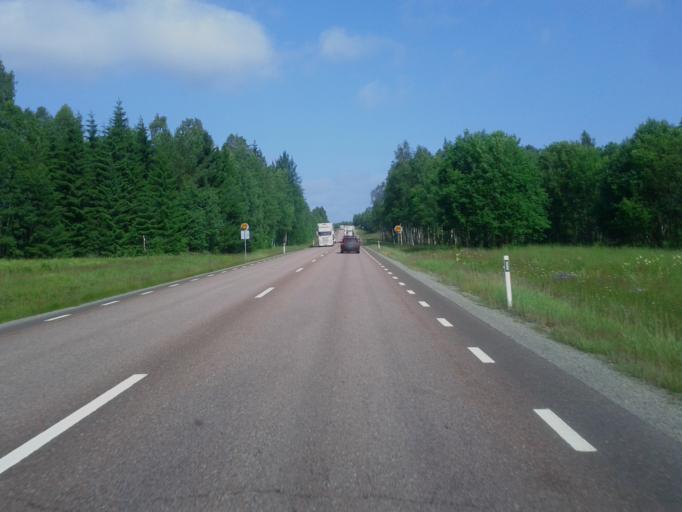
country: SE
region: Vaesterbotten
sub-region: Skelleftea Kommun
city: Burea
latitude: 64.6213
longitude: 21.1785
